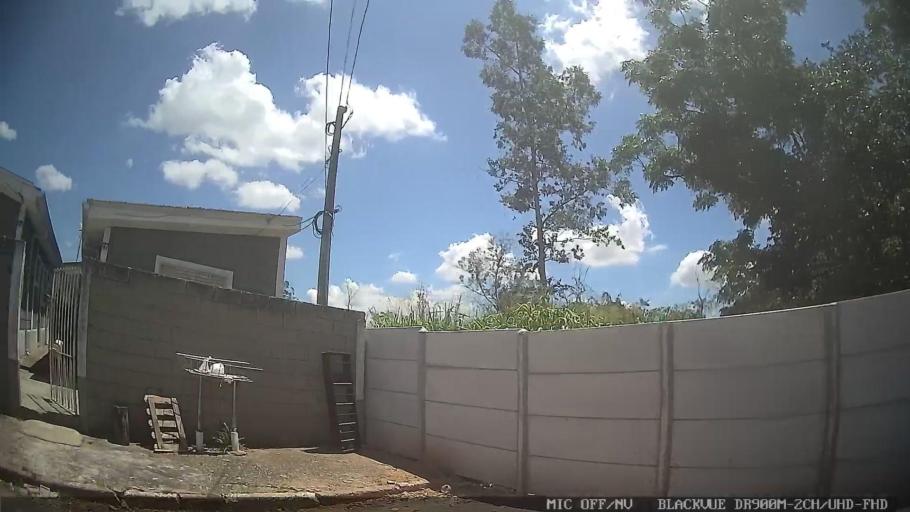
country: BR
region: Sao Paulo
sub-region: Atibaia
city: Atibaia
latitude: -23.1076
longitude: -46.5541
